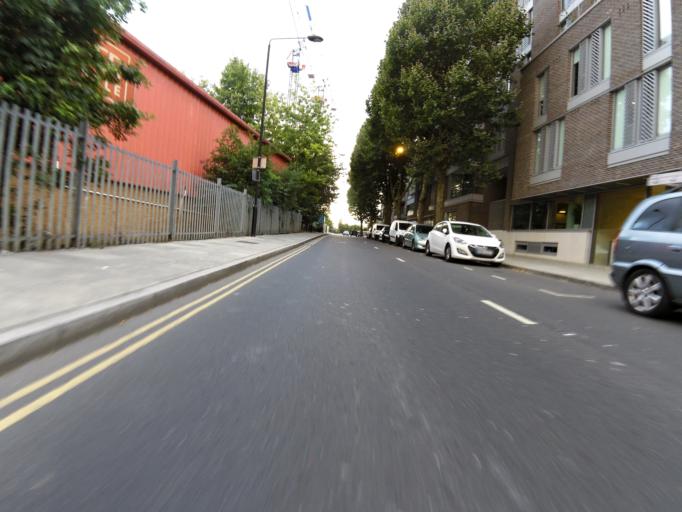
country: GB
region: England
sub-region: Greater London
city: Camden Town
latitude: 51.5385
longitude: -0.1309
